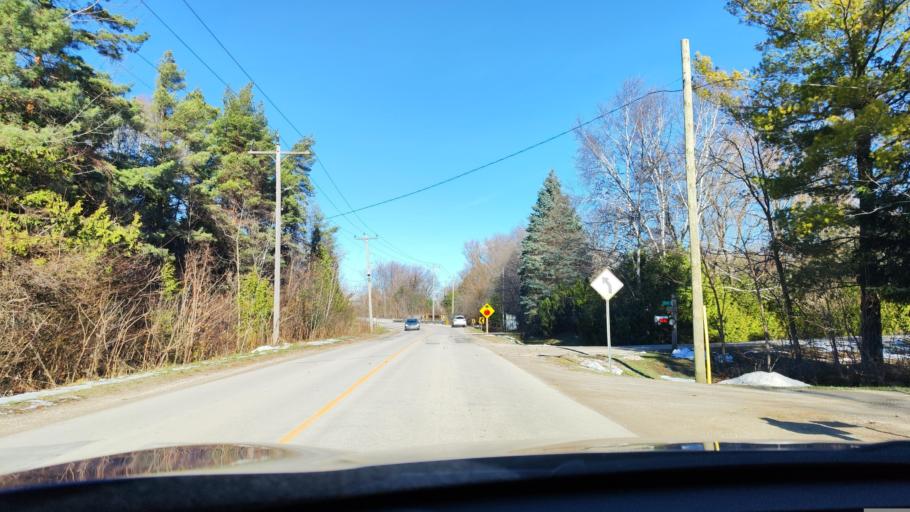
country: CA
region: Ontario
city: Collingwood
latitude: 44.4645
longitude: -80.1737
